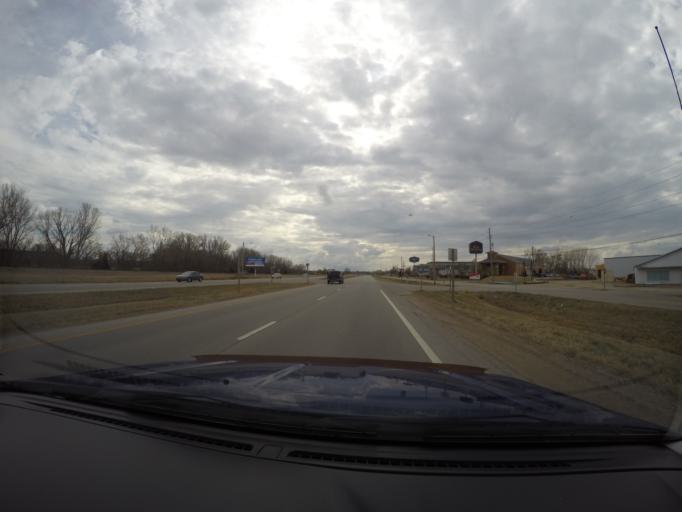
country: US
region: Kansas
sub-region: Riley County
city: Manhattan
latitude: 39.1871
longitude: -96.5473
